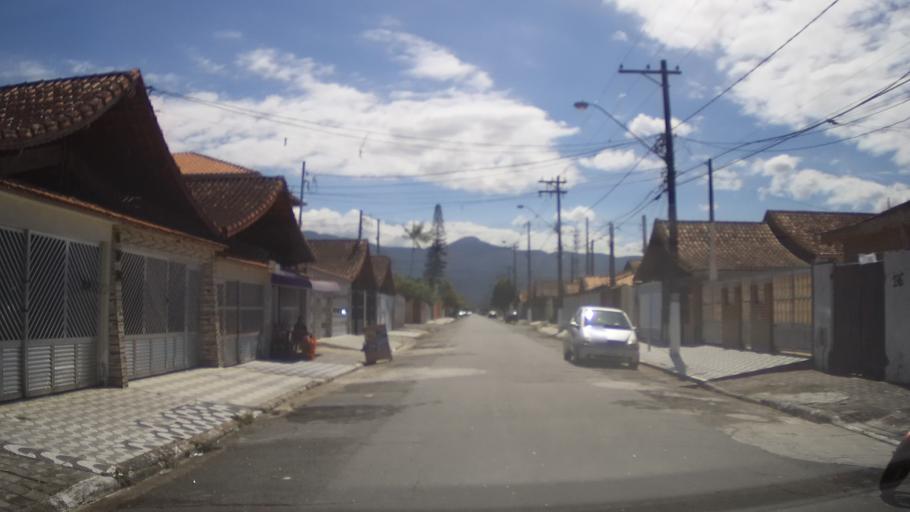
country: BR
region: Sao Paulo
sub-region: Praia Grande
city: Praia Grande
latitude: -24.0385
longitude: -46.5005
